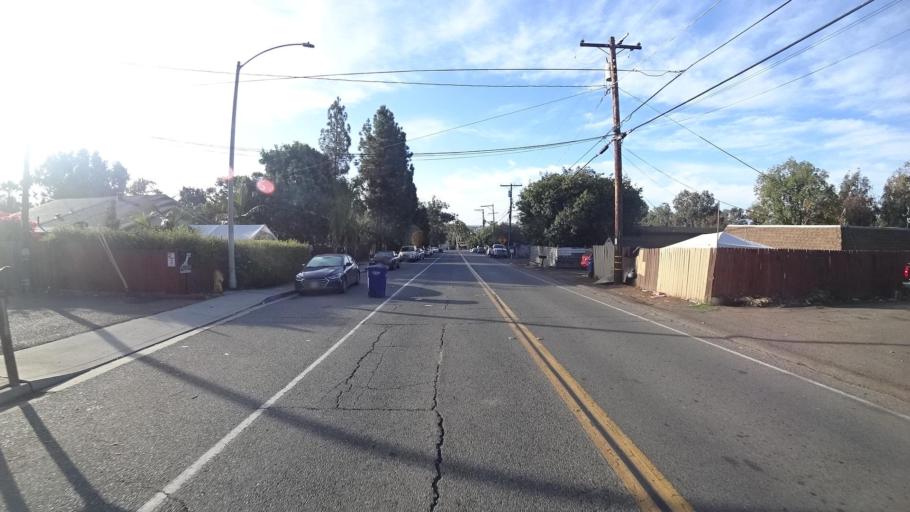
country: US
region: California
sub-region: San Diego County
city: La Presa
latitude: 32.7164
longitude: -117.0095
